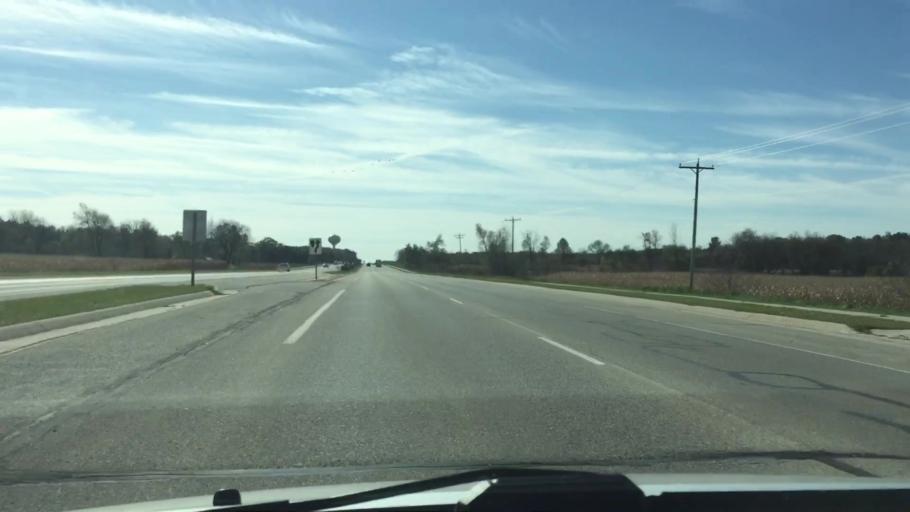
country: US
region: Wisconsin
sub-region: Waukesha County
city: Sussex
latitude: 43.1305
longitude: -88.2442
